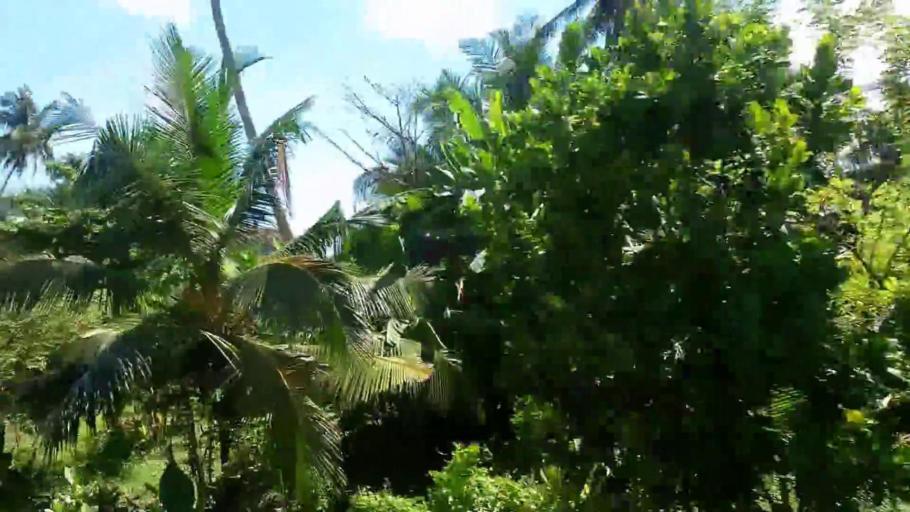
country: LK
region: Southern
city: Hikkaduwa
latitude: 6.1601
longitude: 80.0940
